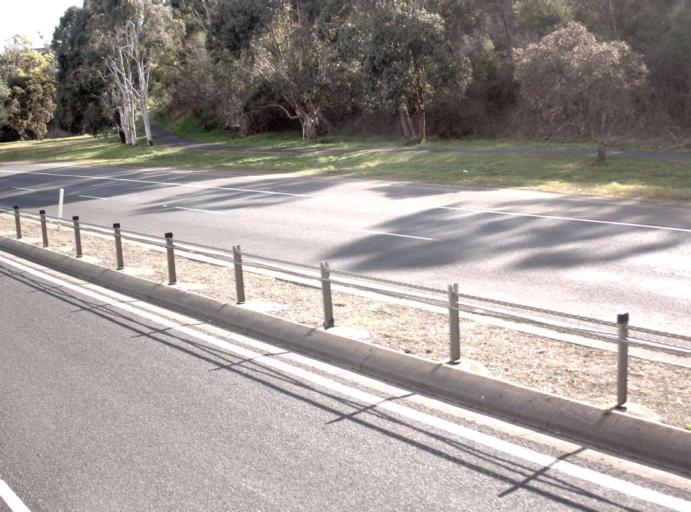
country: AU
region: Tasmania
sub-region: Launceston
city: Newnham
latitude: -41.4078
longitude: 147.1246
